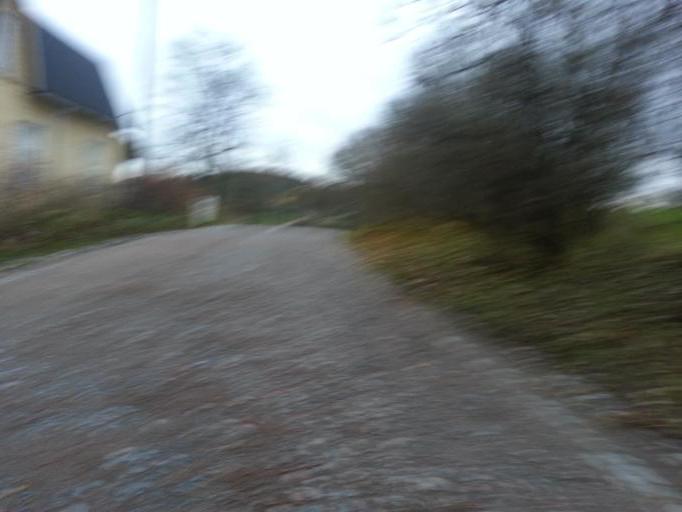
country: FI
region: Uusimaa
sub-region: Helsinki
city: Helsinki
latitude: 60.1420
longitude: 24.9861
